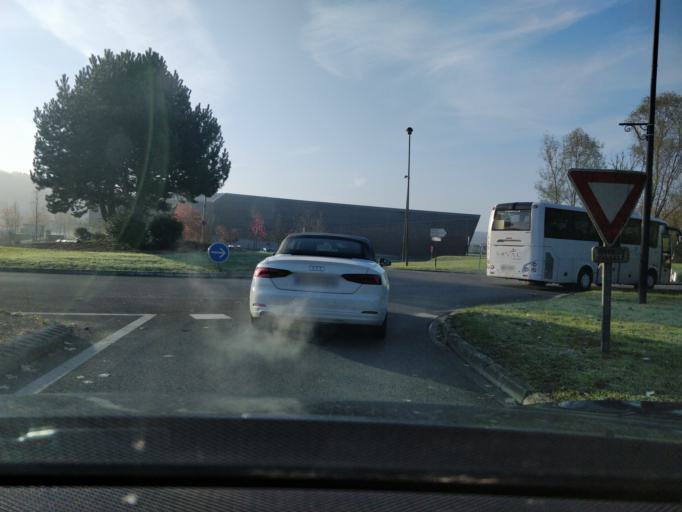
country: FR
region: Ile-de-France
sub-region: Departement de l'Essonne
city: Limours
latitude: 48.6298
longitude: 2.0809
